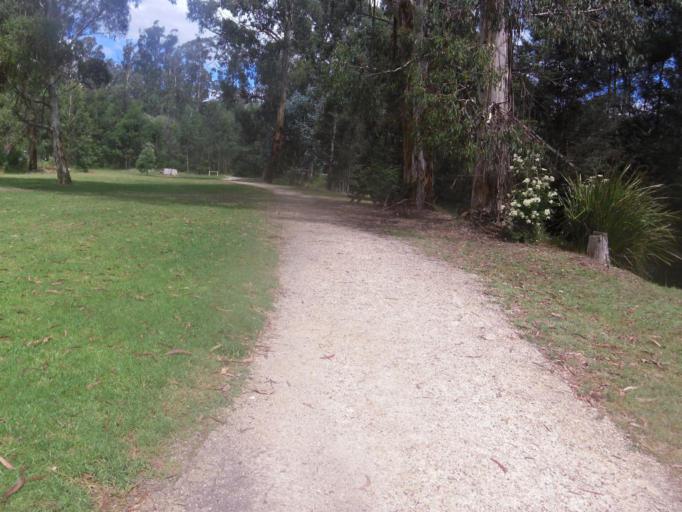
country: AU
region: Victoria
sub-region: Yarra Ranges
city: Millgrove
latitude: -37.5103
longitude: 145.7495
